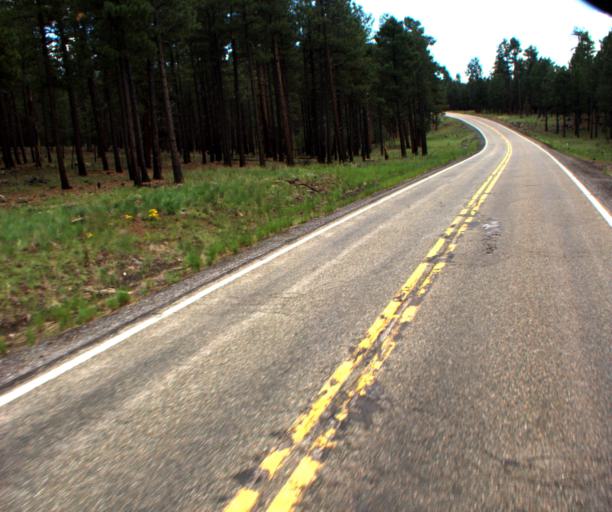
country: US
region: Arizona
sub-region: Coconino County
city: Parks
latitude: 35.3339
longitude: -111.7827
